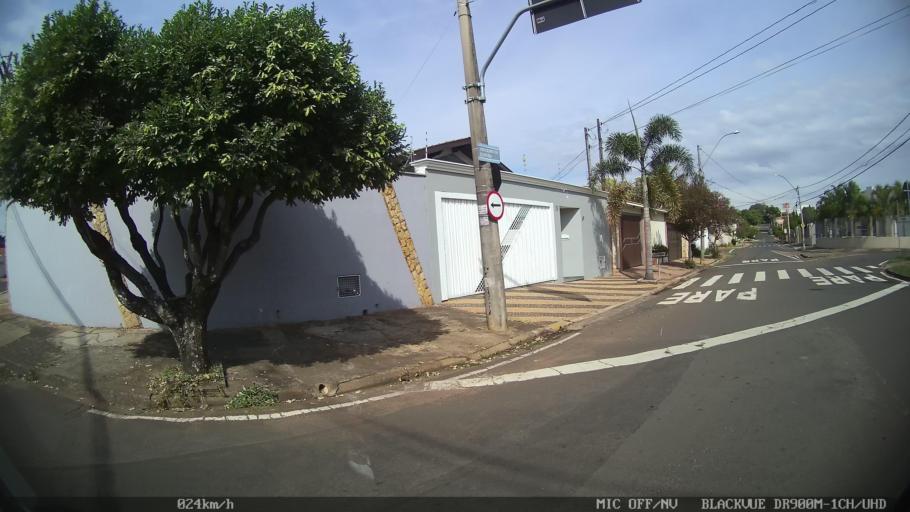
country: BR
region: Sao Paulo
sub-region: Piracicaba
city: Piracicaba
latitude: -22.7153
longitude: -47.6664
